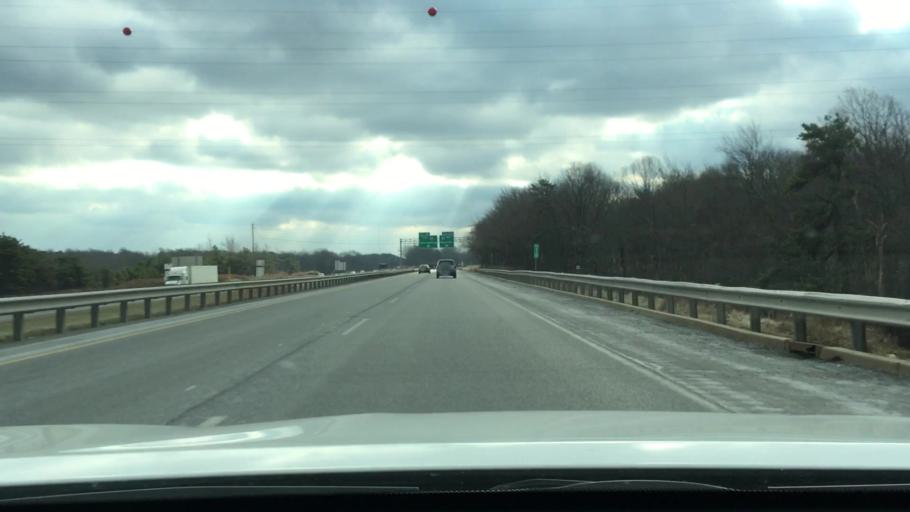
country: US
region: Pennsylvania
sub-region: Monroe County
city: Emerald Lakes
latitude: 41.0931
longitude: -75.3965
